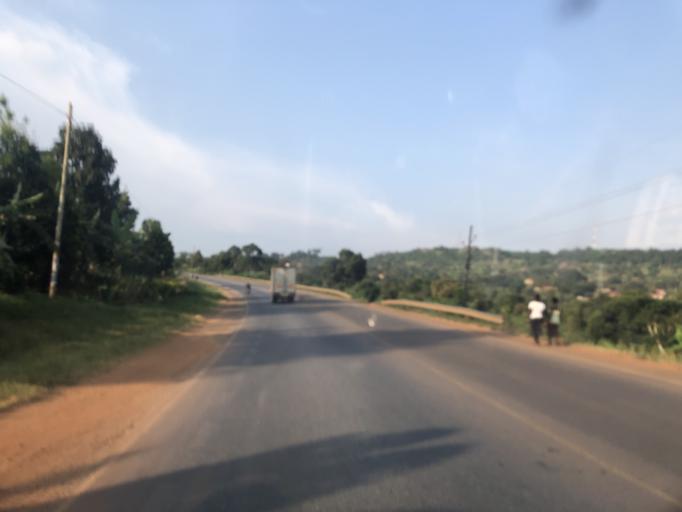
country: UG
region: Central Region
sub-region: Mpigi District
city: Mpigi
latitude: 0.1395
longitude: 32.2200
